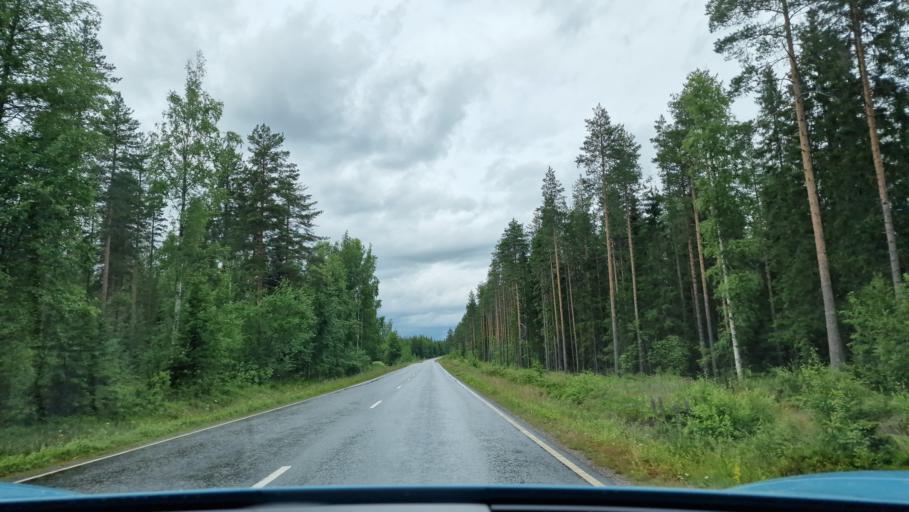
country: FI
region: Central Finland
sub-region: Saarijaervi-Viitasaari
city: Pylkoenmaeki
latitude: 62.6745
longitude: 24.5081
